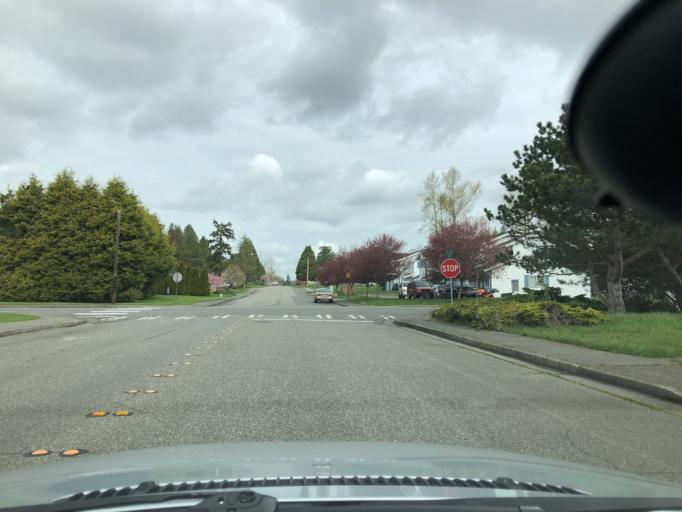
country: US
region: Washington
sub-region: Whatcom County
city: Blaine
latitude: 48.9977
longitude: -122.7400
